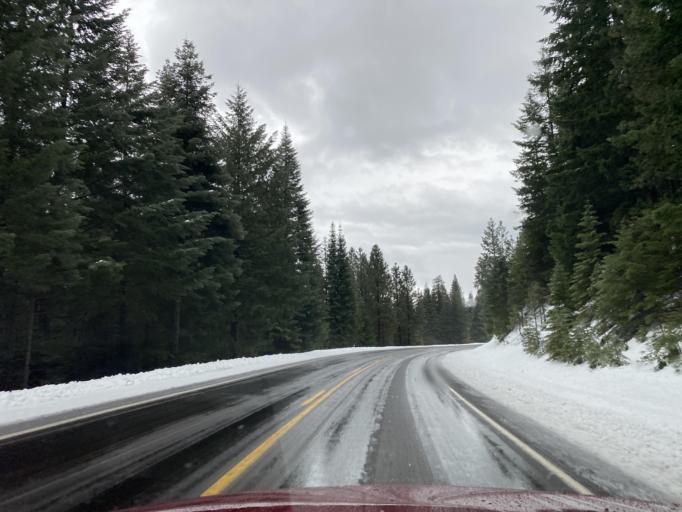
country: US
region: Oregon
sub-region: Klamath County
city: Klamath Falls
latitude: 42.5226
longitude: -122.0852
